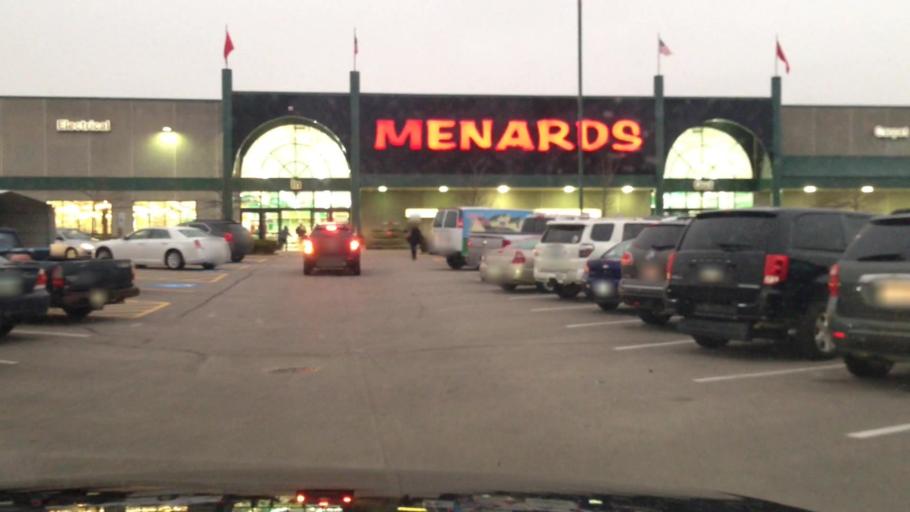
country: US
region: Illinois
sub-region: Kane County
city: Gilberts
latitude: 42.1236
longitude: -88.3370
